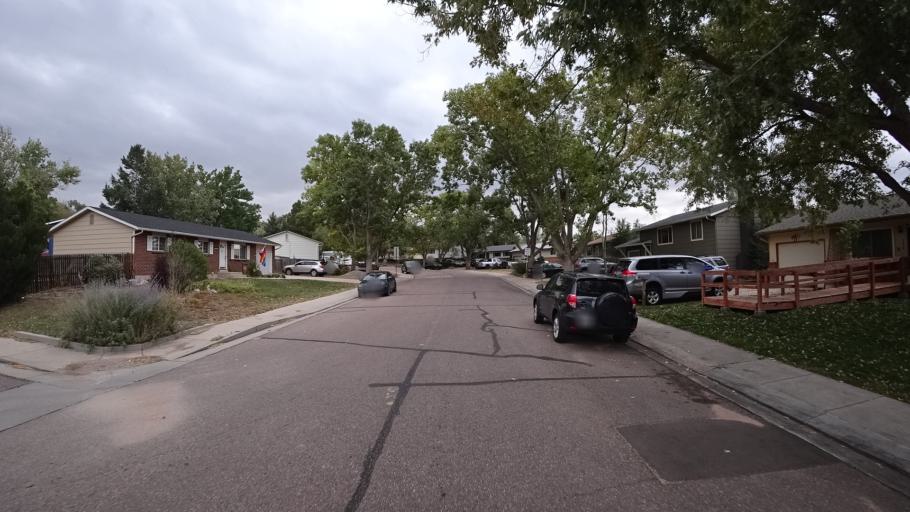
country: US
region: Colorado
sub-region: El Paso County
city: Cimarron Hills
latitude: 38.8901
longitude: -104.7417
